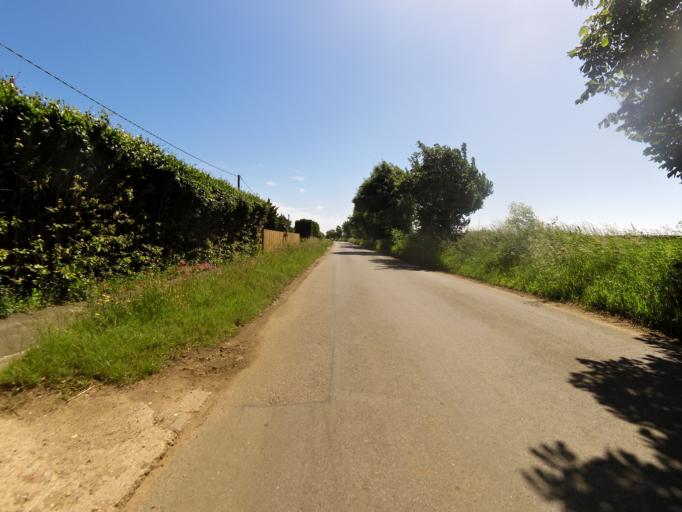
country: GB
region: England
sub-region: Suffolk
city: Wickham Market
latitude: 52.0586
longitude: 1.4393
